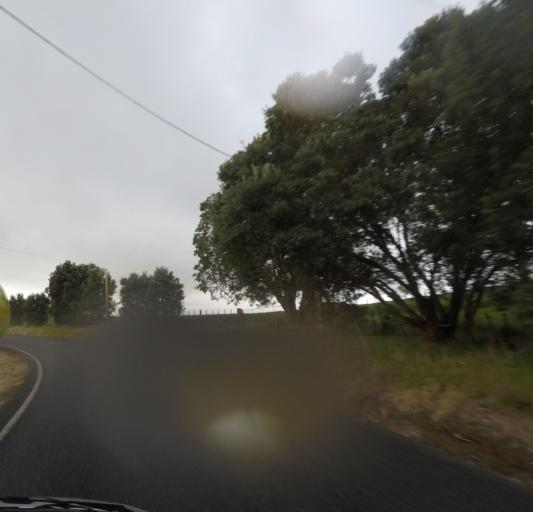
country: NZ
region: Auckland
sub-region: Auckland
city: Warkworth
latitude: -36.3776
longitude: 174.7600
